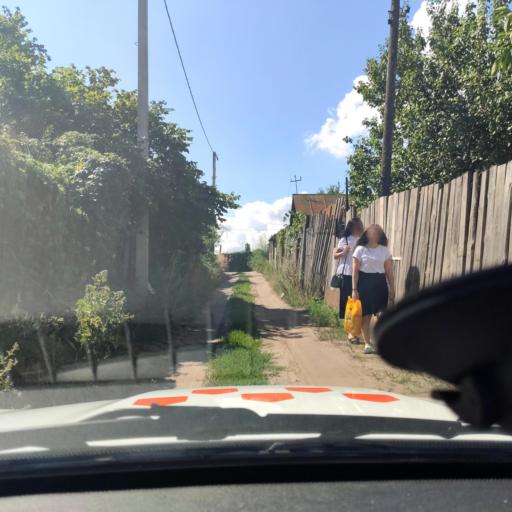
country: RU
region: Voronezj
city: Maslovka
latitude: 51.5981
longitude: 39.2321
